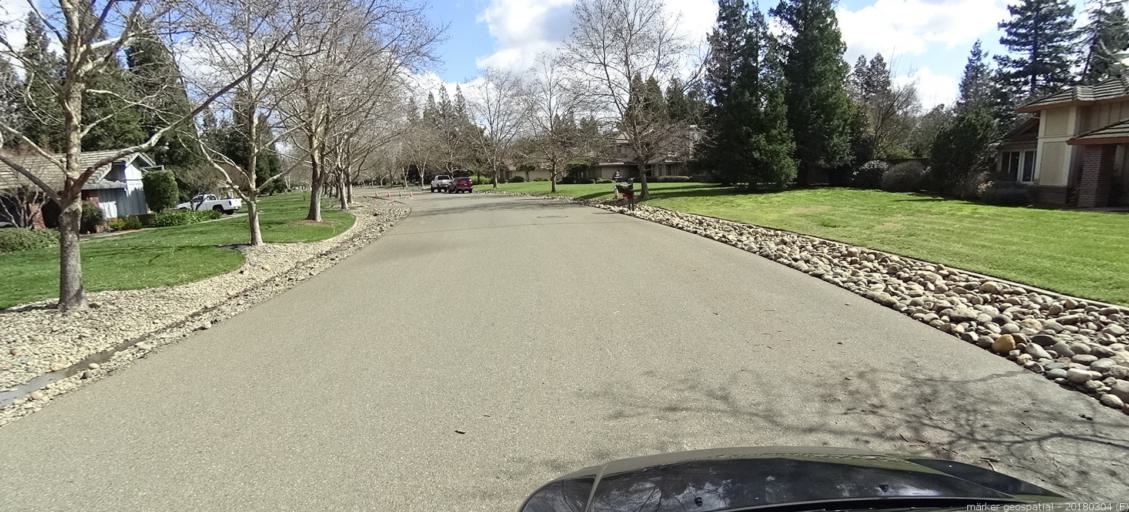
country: US
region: California
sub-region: Sacramento County
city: Vineyard
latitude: 38.4535
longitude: -121.3137
